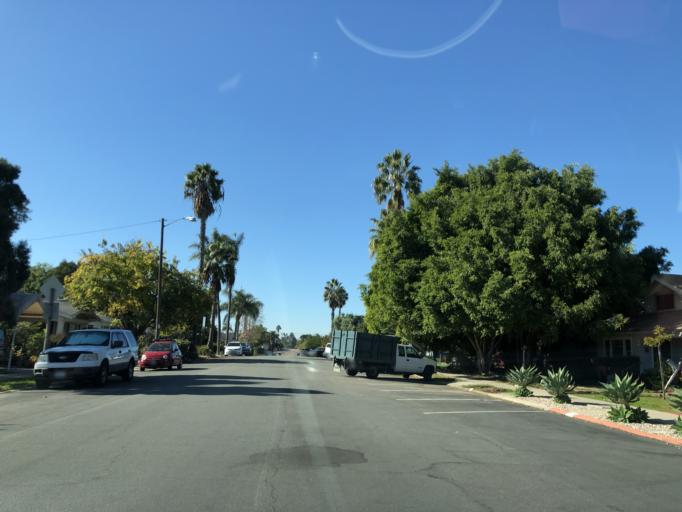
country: US
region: California
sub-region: San Diego County
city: San Diego
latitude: 32.7276
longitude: -117.1256
